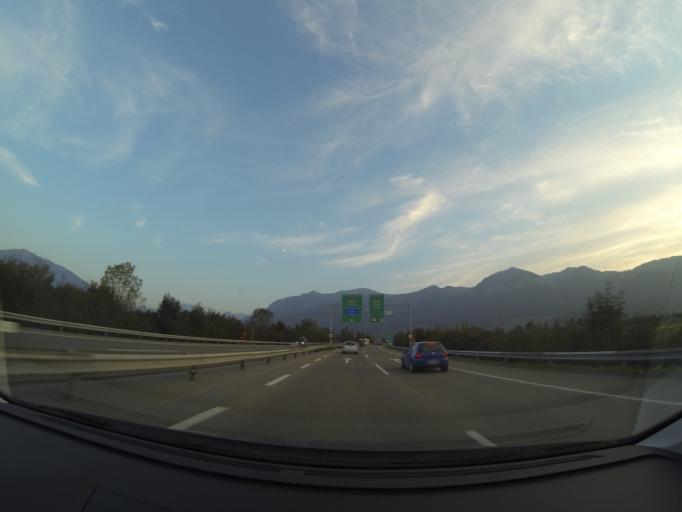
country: CH
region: Schwyz
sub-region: Bezirk March
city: Reichenburg
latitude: 47.1868
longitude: 8.9765
